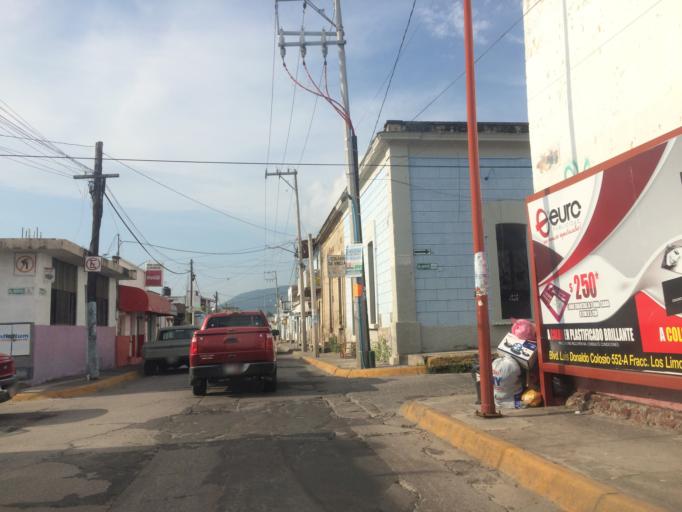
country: MX
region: Nayarit
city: Xalisco
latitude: 21.4430
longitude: -104.9000
